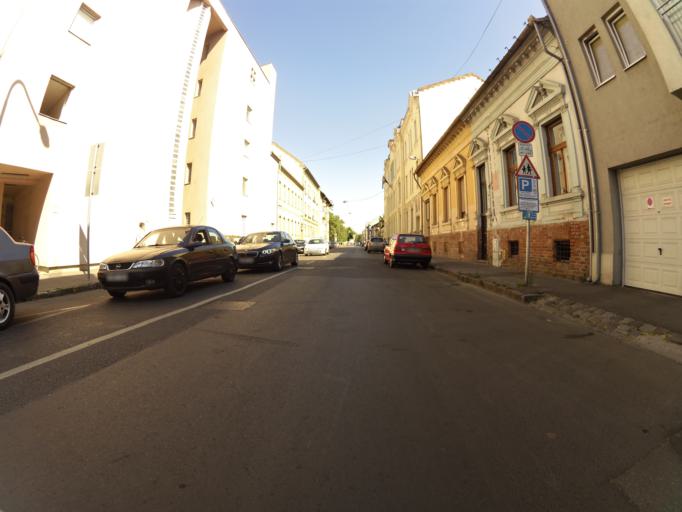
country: HU
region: Csongrad
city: Szeged
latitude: 46.2593
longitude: 20.1451
